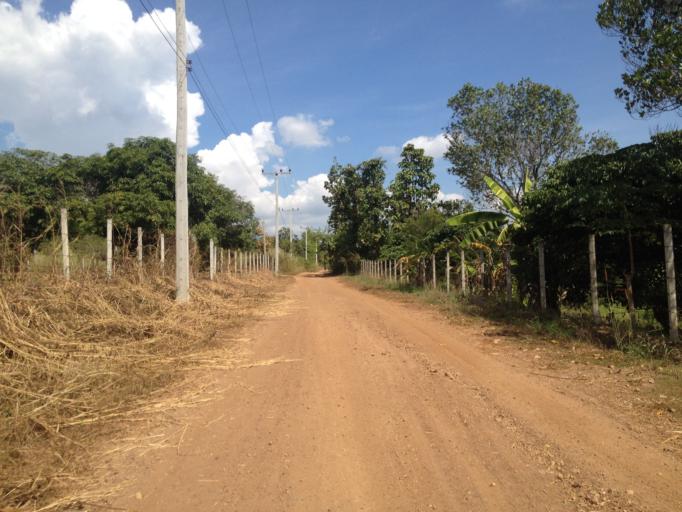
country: TH
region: Chiang Mai
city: Hang Dong
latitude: 18.7101
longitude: 98.8721
